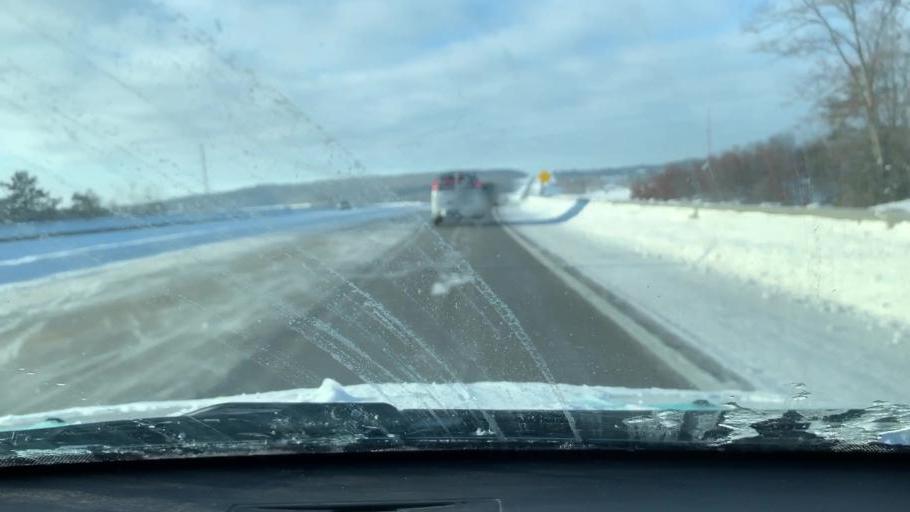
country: US
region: Michigan
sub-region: Wexford County
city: Cadillac
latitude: 44.2372
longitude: -85.3716
